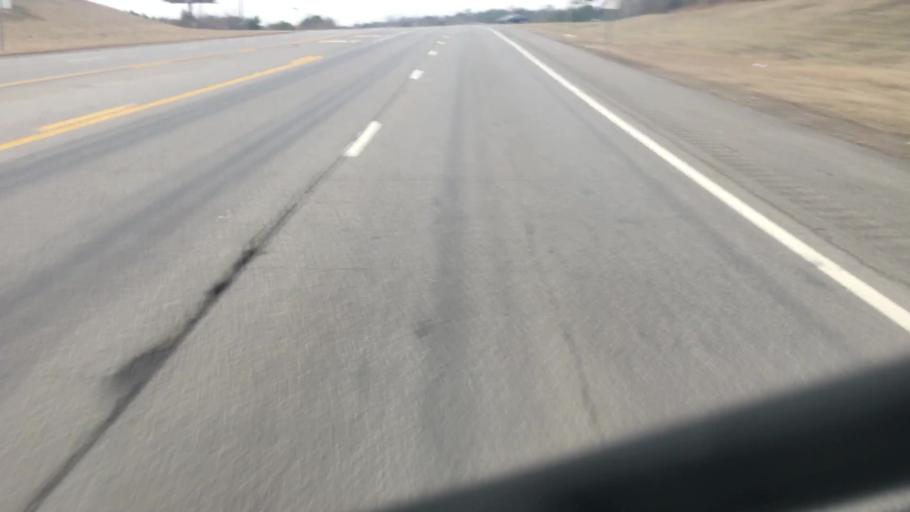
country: US
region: Alabama
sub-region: Walker County
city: Jasper
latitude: 33.7986
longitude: -87.2374
